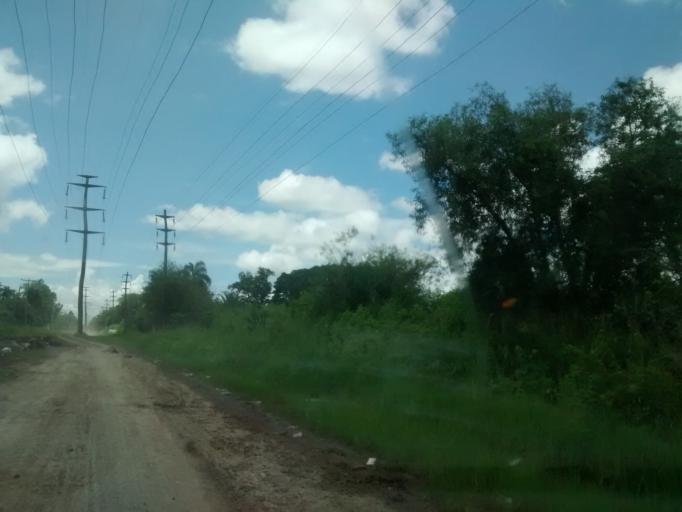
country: AR
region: Chaco
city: Fontana
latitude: -27.4155
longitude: -58.9837
